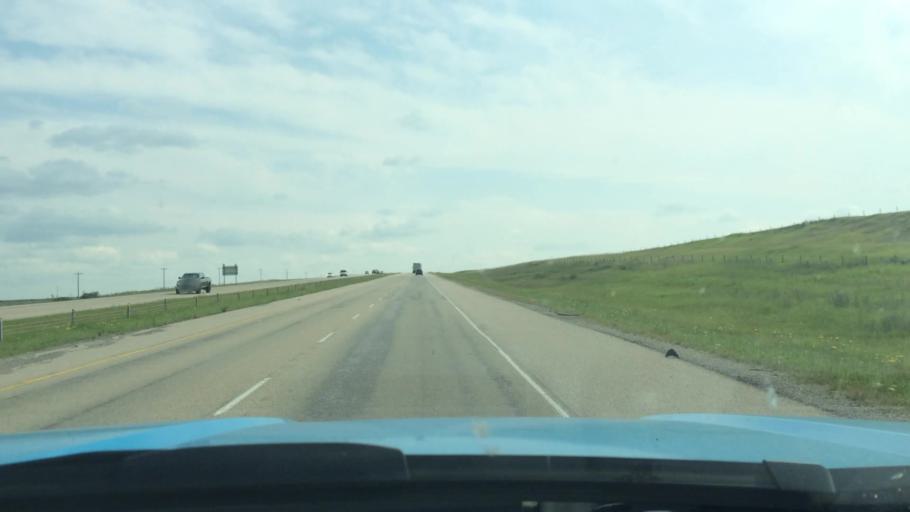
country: CA
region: Alberta
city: Carstairs
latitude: 51.5474
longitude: -114.0254
